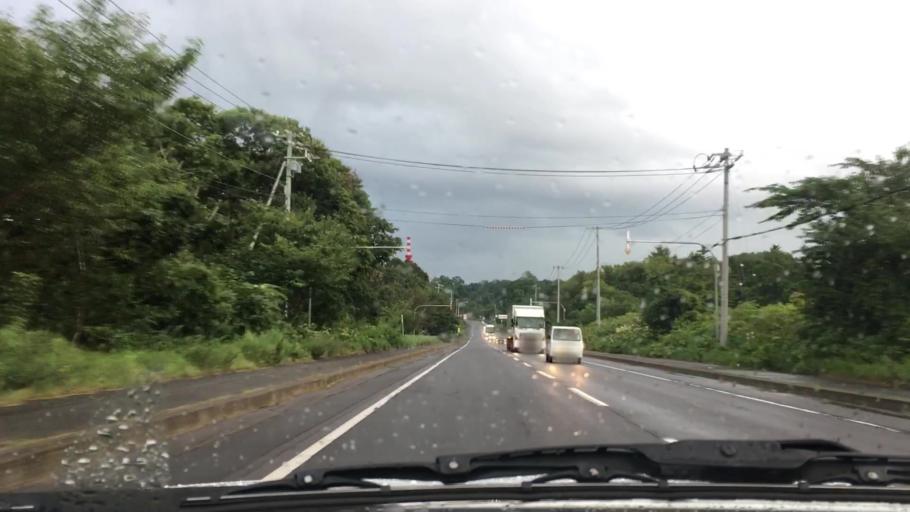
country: JP
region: Hokkaido
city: Nanae
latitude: 42.0868
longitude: 140.5835
